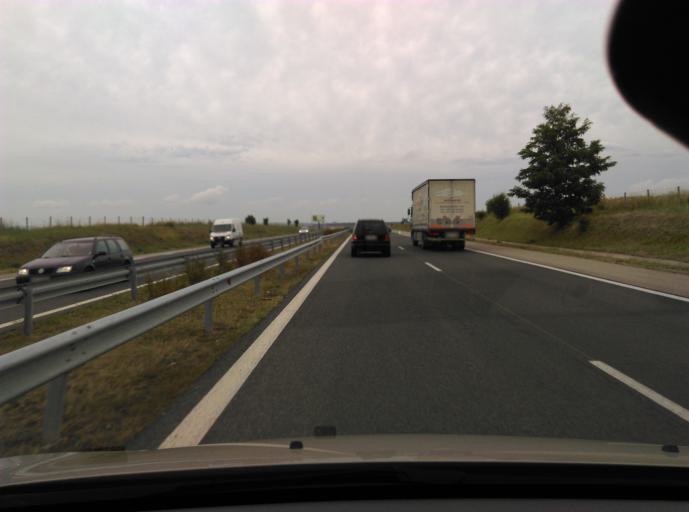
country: BG
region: Stara Zagora
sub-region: Obshtina Chirpan
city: Chirpan
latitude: 42.1950
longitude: 25.2448
